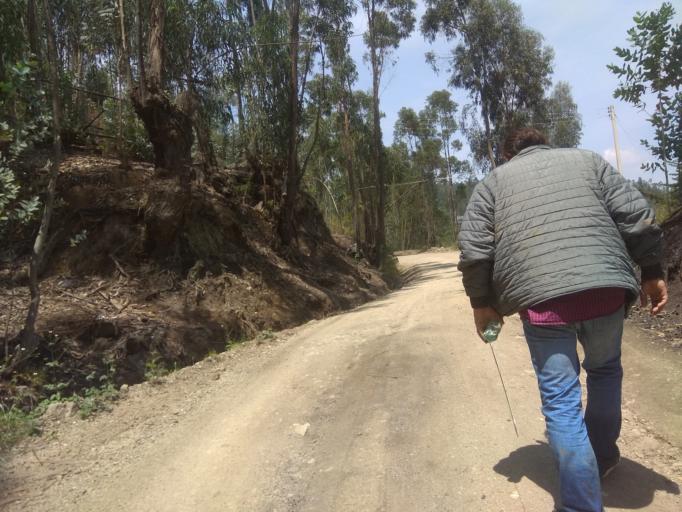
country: CO
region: Boyaca
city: Socha Viejo
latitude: 5.9787
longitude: -72.7267
